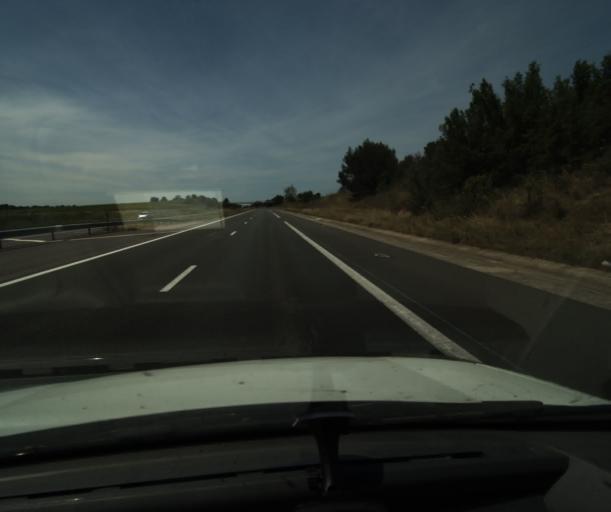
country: FR
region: Languedoc-Roussillon
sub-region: Departement de l'Aude
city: Trebes
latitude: 43.1872
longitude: 2.4676
